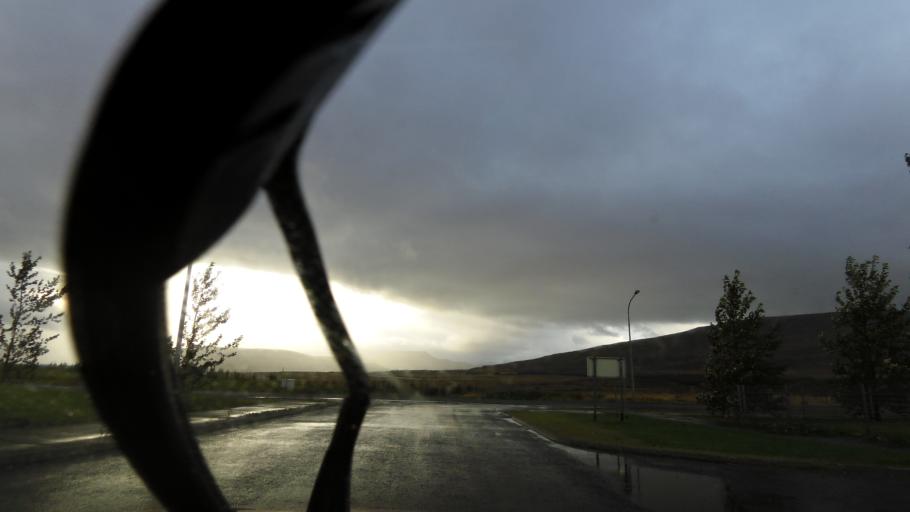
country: IS
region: West
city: Borgarnes
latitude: 64.3812
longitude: -21.8395
